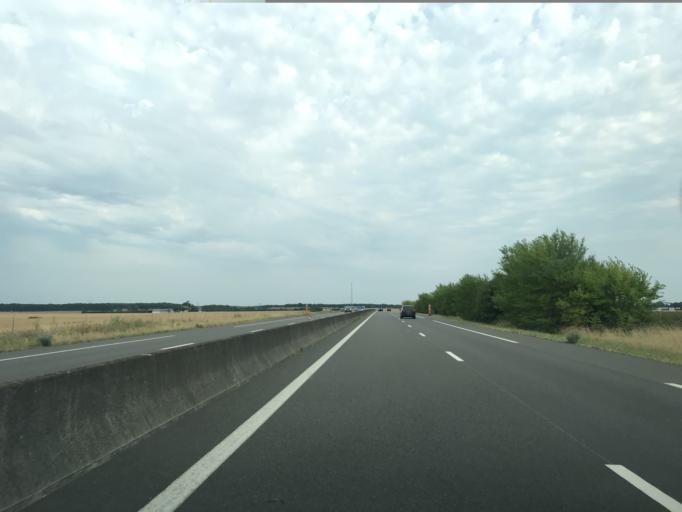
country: FR
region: Centre
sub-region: Departement d'Indre-et-Loire
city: Neuvy-le-Roi
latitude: 47.5663
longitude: 0.5878
